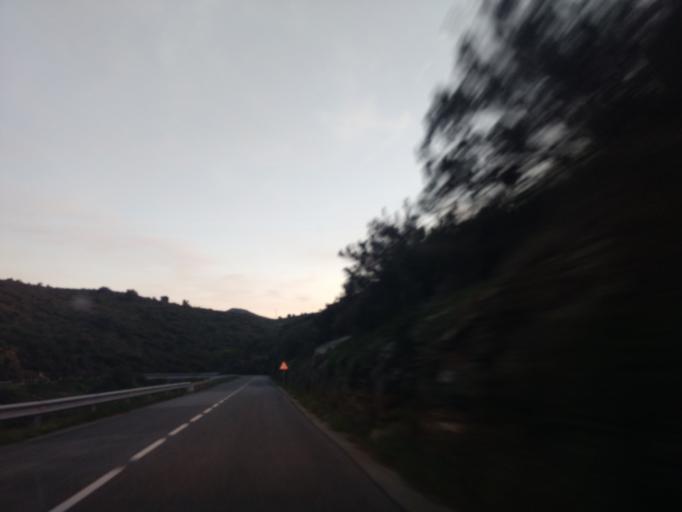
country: ES
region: Catalonia
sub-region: Provincia de Girona
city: Roses
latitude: 42.2883
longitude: 3.2216
